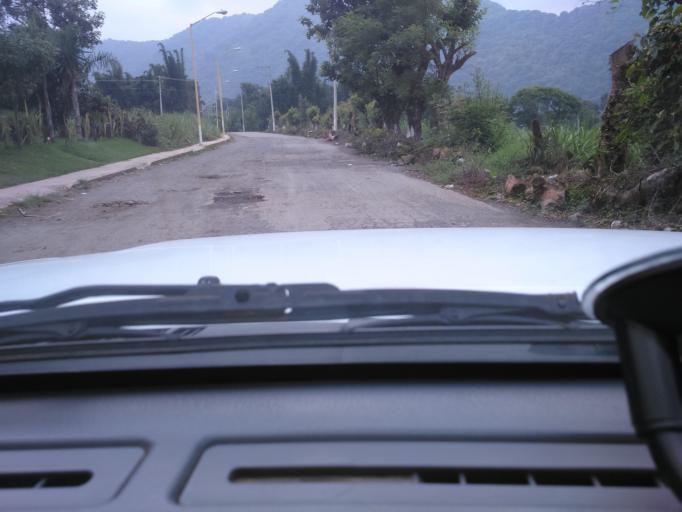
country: MX
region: Veracruz
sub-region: Mariano Escobedo
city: Chicola
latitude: 18.8987
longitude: -97.1076
